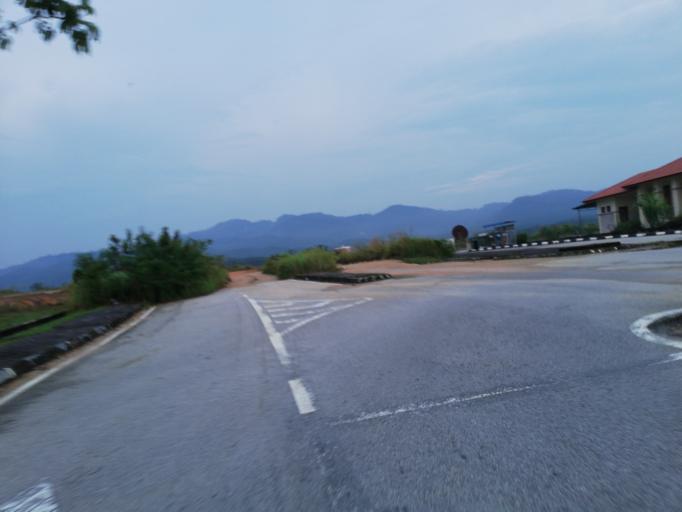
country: MY
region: Kedah
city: Kulim
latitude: 5.3861
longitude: 100.5823
